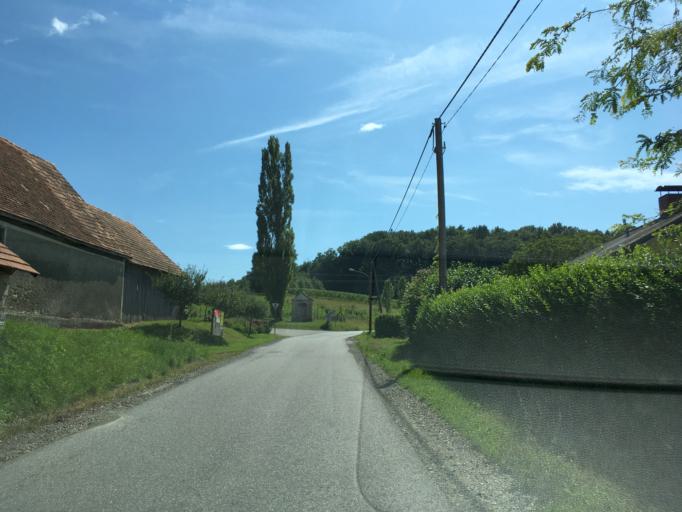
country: AT
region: Styria
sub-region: Politischer Bezirk Leibnitz
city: Sankt Nikolai im Sausal
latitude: 46.8031
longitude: 15.4342
